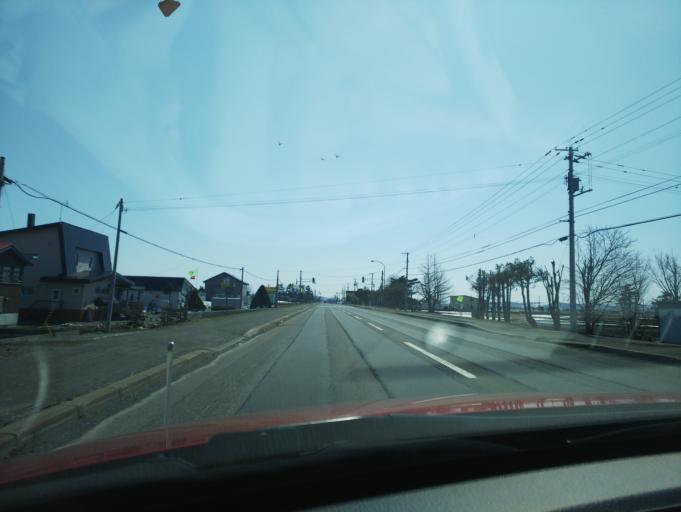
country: JP
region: Hokkaido
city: Nayoro
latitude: 44.2131
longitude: 142.3949
